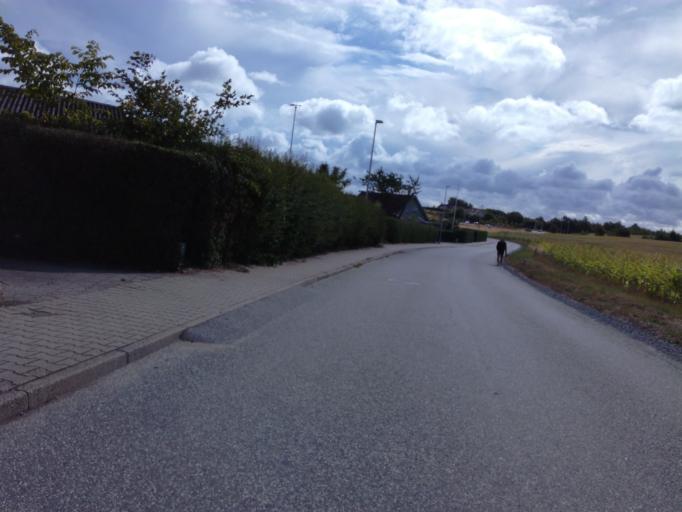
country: DK
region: South Denmark
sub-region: Fredericia Kommune
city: Fredericia
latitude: 55.6091
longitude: 9.7504
